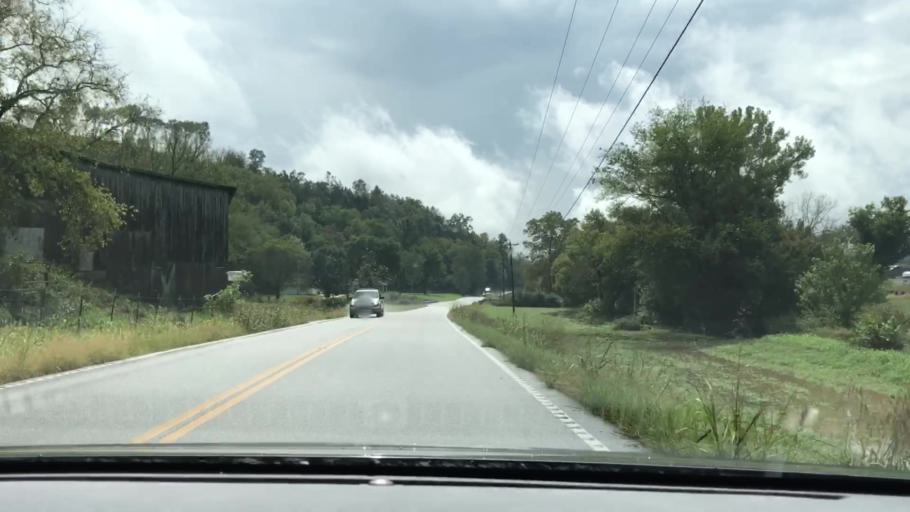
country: US
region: Tennessee
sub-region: Smith County
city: Carthage
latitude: 36.3294
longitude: -85.9652
